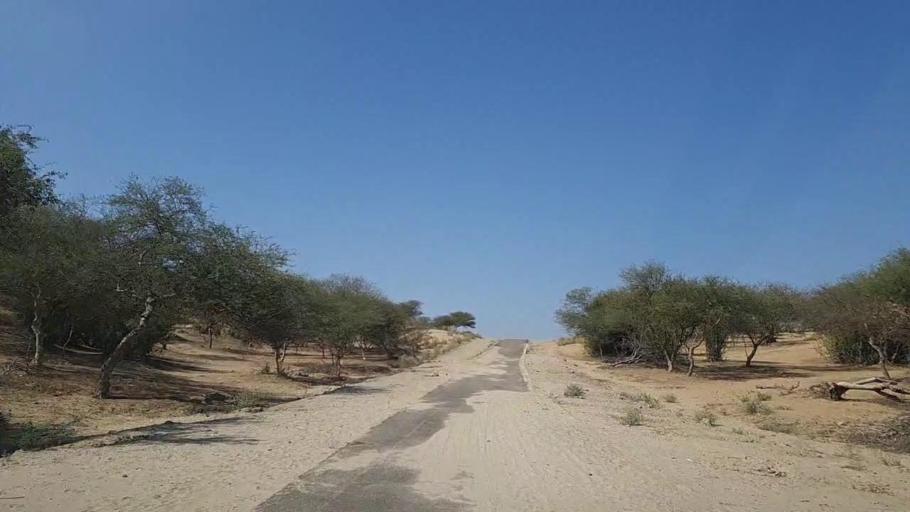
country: PK
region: Sindh
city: Mithi
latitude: 24.7568
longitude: 69.7789
